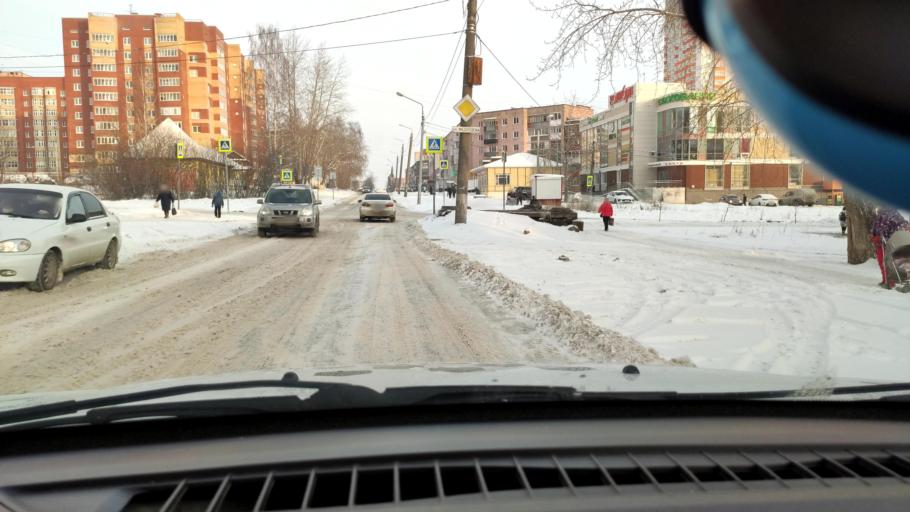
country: RU
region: Perm
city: Perm
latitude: 58.1004
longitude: 56.2947
